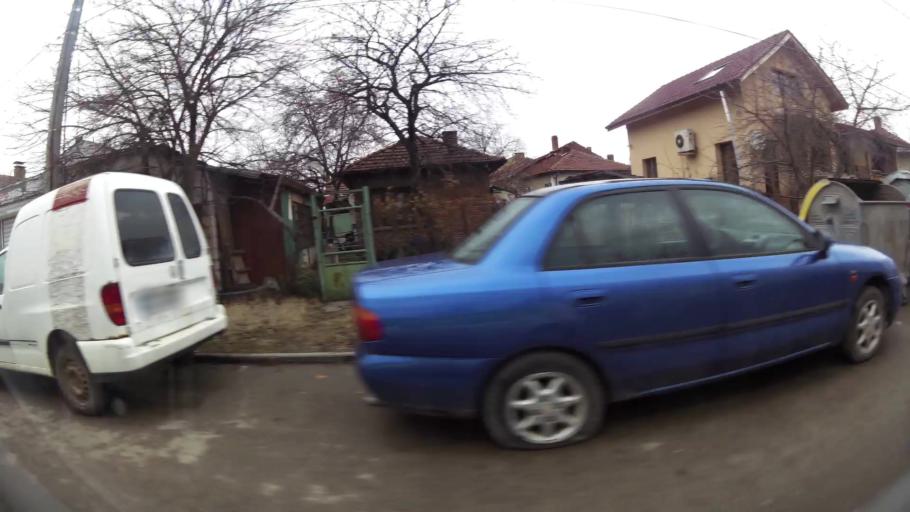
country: BG
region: Sofia-Capital
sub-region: Stolichna Obshtina
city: Sofia
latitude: 42.7258
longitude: 23.2693
